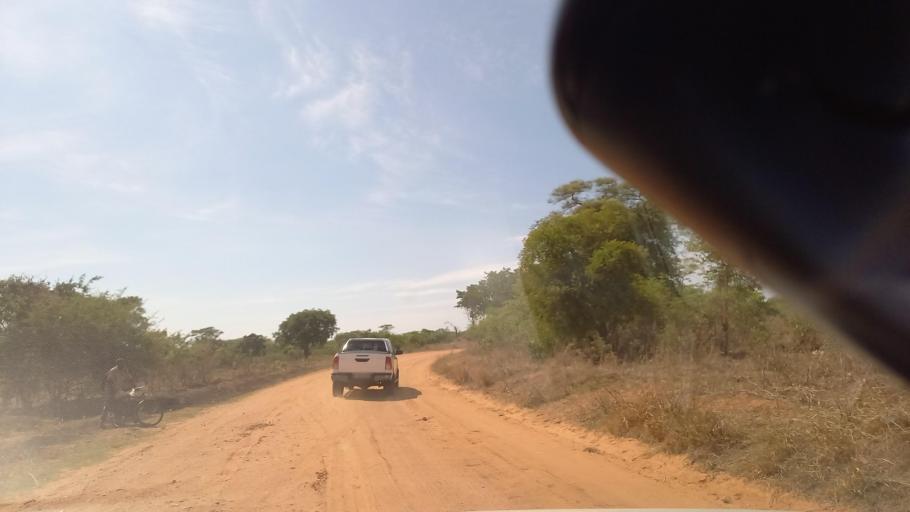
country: ZM
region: Southern
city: Mazabuka
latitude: -16.0338
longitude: 27.6171
